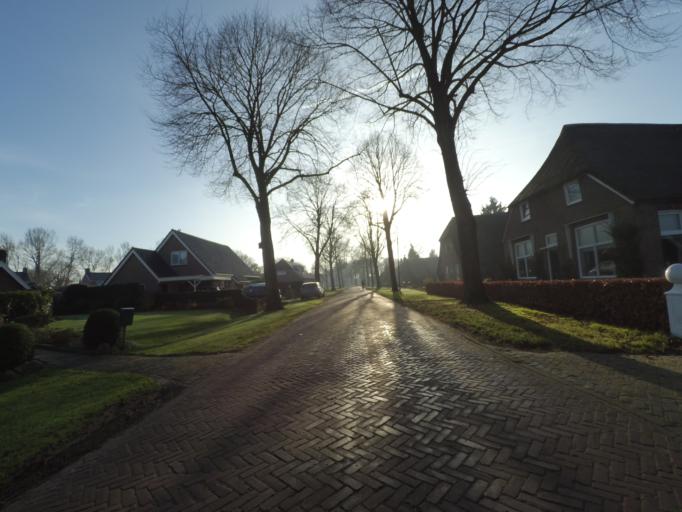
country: NL
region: Drenthe
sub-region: Gemeente Assen
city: Assen
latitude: 52.8797
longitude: 6.6443
